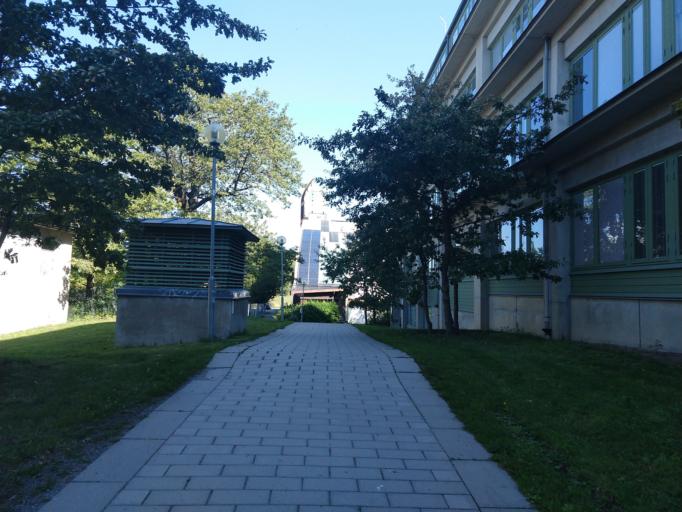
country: SE
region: Stockholm
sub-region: Norrtalje Kommun
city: Bergshamra
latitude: 59.3658
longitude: 18.0568
